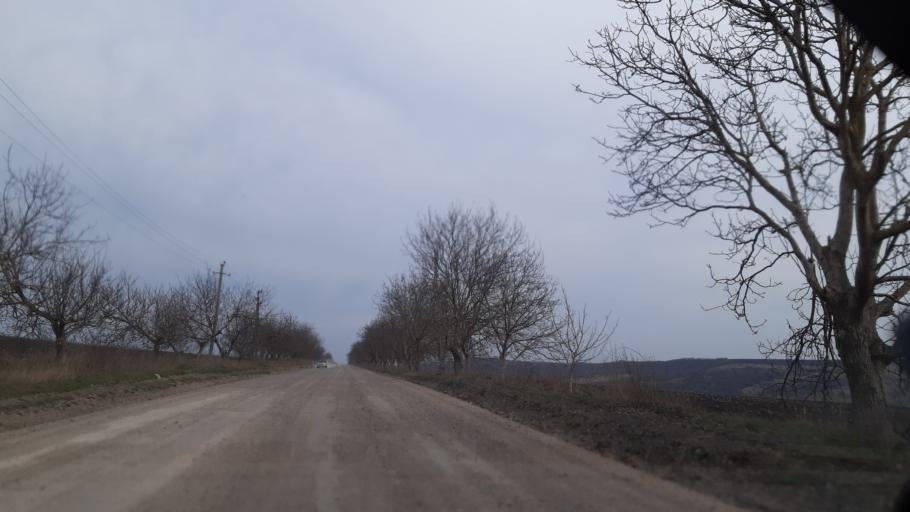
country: MD
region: Soldanesti
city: Soldanesti
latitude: 47.6957
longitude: 28.7316
